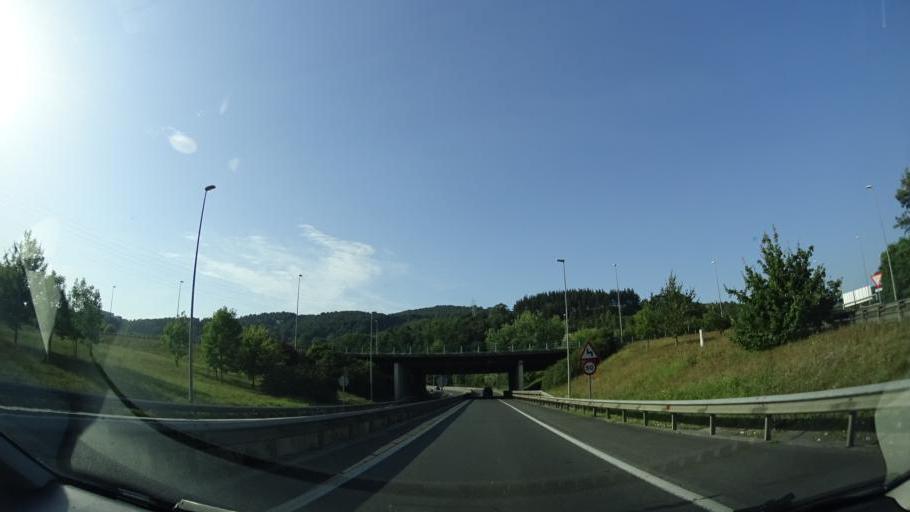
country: ES
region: Basque Country
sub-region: Bizkaia
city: Galdakao
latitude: 43.2290
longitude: -2.8210
